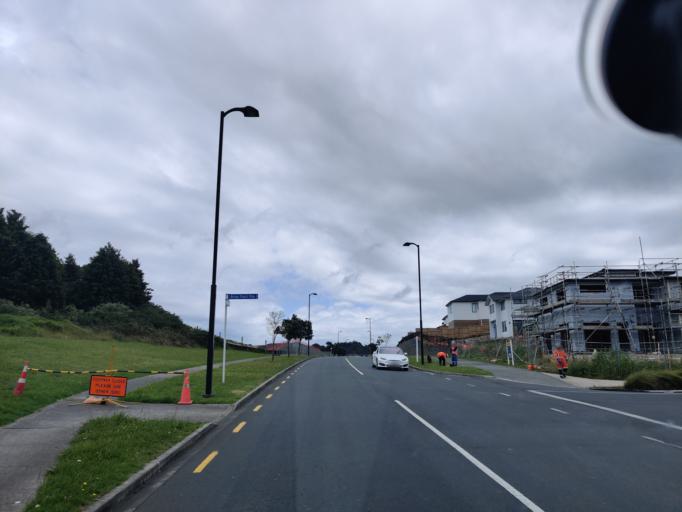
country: NZ
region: Auckland
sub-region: Auckland
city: Rothesay Bay
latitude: -36.5952
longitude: 174.6711
